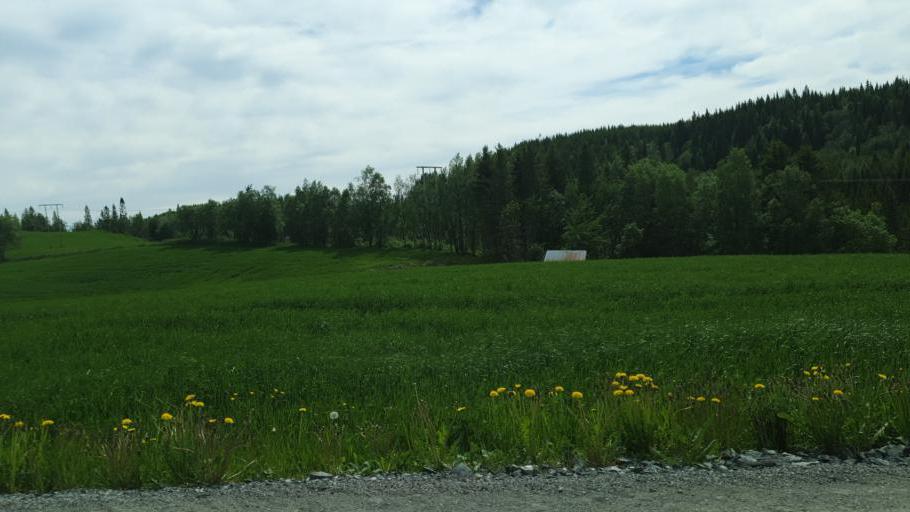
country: NO
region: Nord-Trondelag
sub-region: Leksvik
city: Leksvik
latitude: 63.6868
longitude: 10.5479
